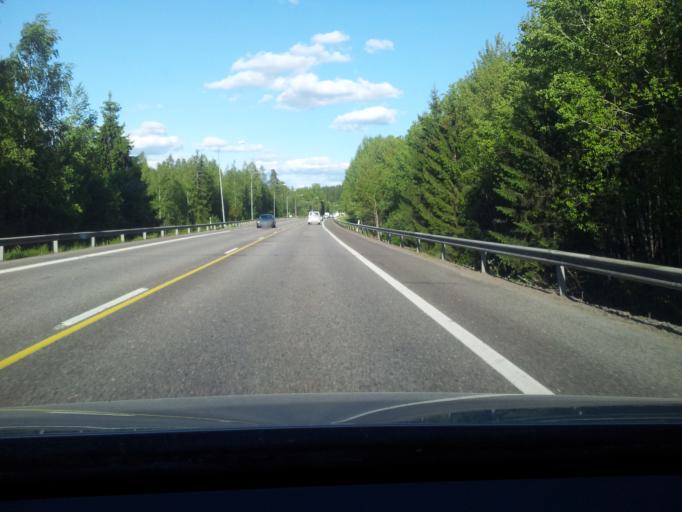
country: FI
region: Kymenlaakso
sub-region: Kouvola
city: Kouvola
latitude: 60.8804
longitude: 26.6906
